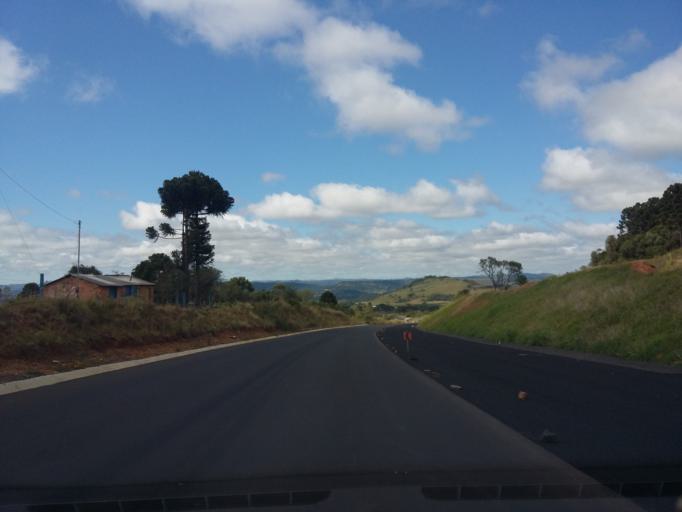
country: BR
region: Santa Catarina
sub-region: Sao Joaquim
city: Sao Joaquim
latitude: -28.0633
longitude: -50.0733
